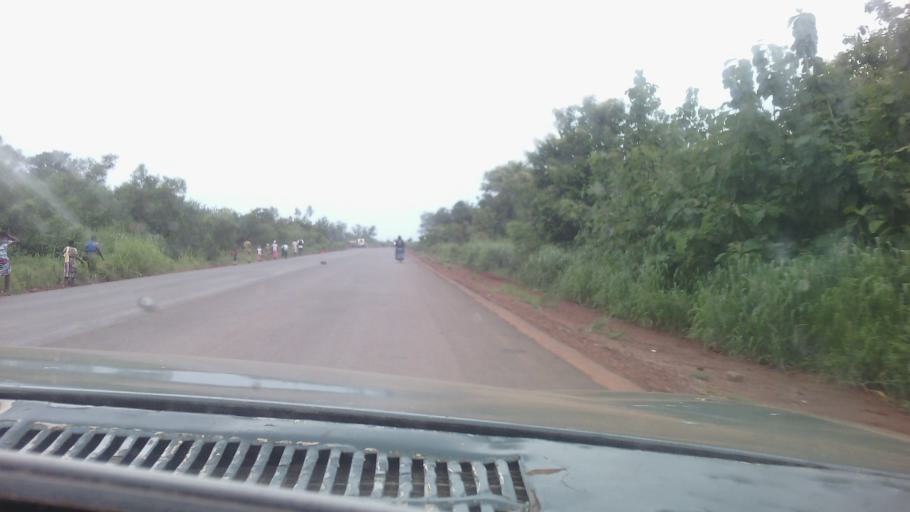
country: BJ
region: Mono
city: Come
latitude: 6.5297
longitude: 1.8184
